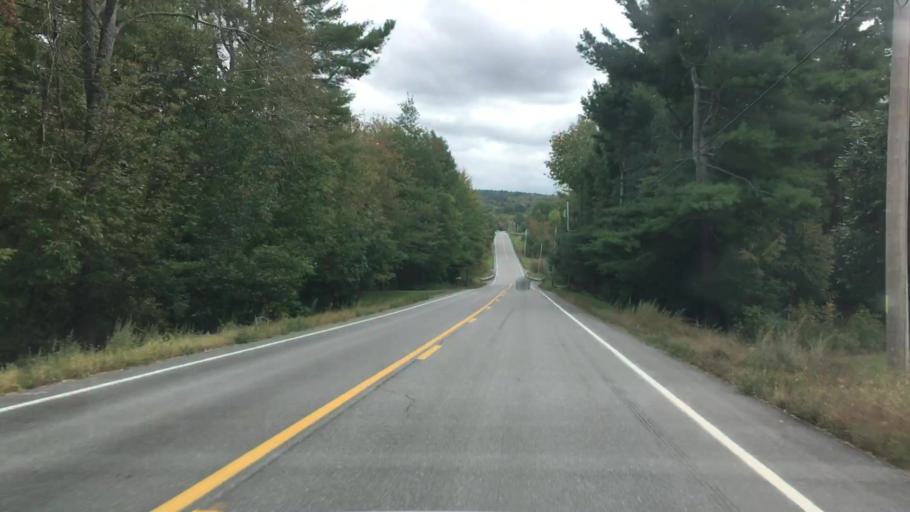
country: US
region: Maine
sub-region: Penobscot County
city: Hermon
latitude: 44.7527
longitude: -68.9713
